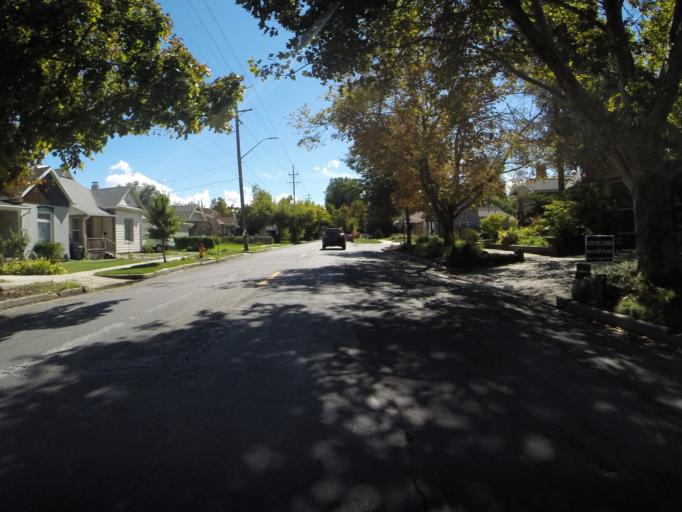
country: US
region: Utah
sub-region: Salt Lake County
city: South Salt Lake
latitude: 40.7302
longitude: -111.8768
